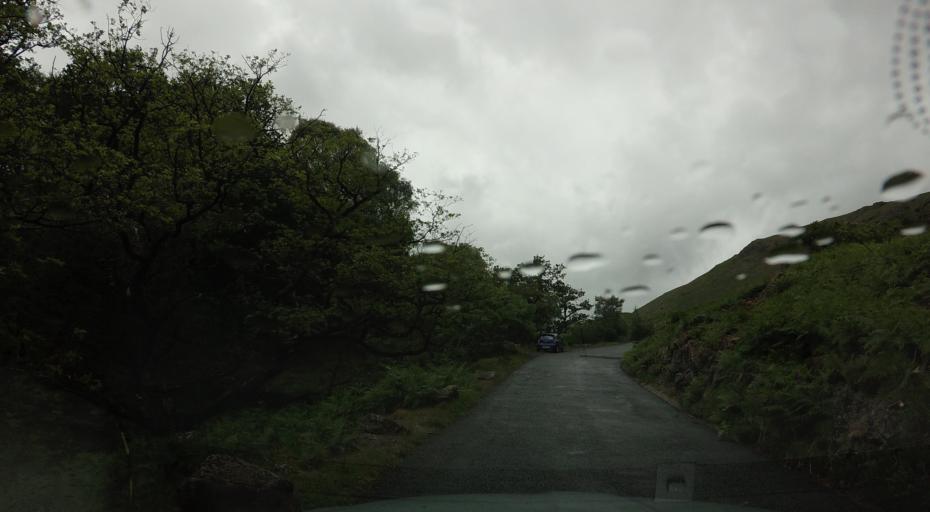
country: GB
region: England
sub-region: Cumbria
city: Keswick
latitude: 54.5147
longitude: -3.1776
